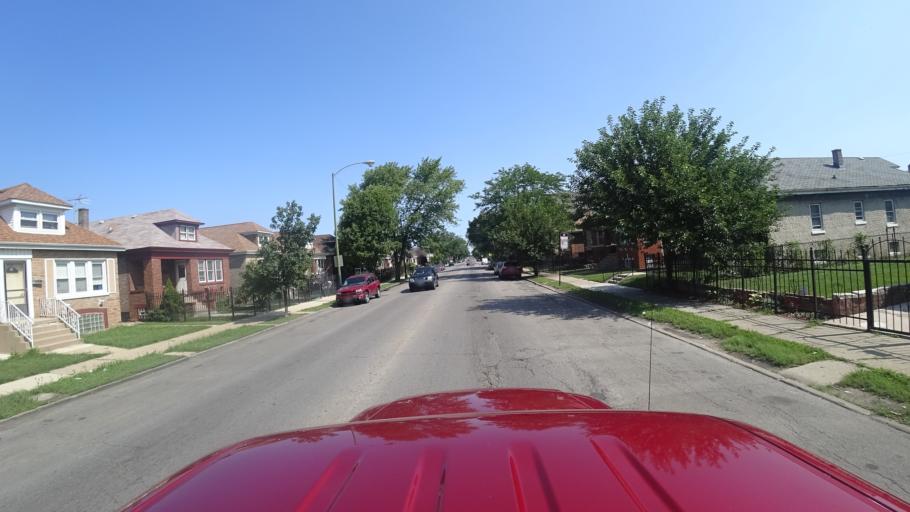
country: US
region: Illinois
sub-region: Cook County
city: Chicago
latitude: 41.7959
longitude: -87.6939
